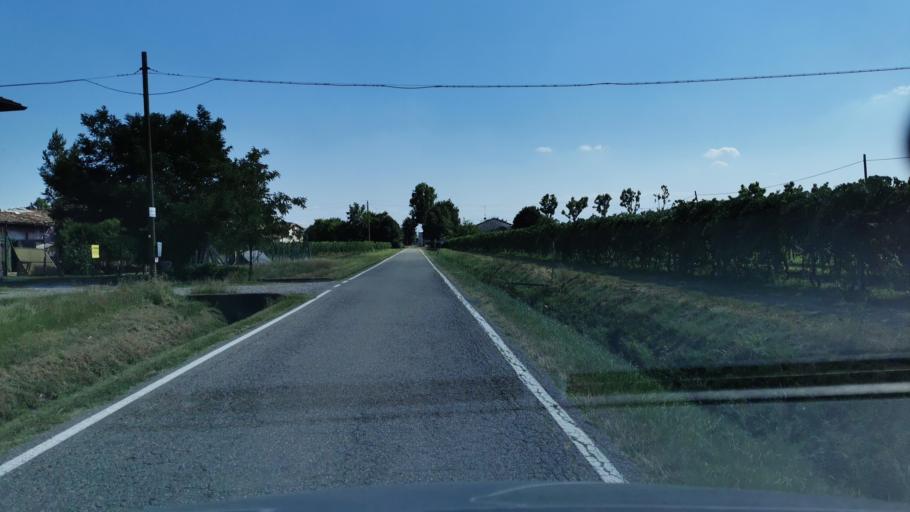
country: IT
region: Emilia-Romagna
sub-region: Provincia di Modena
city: Limidi
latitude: 44.7685
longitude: 10.9168
